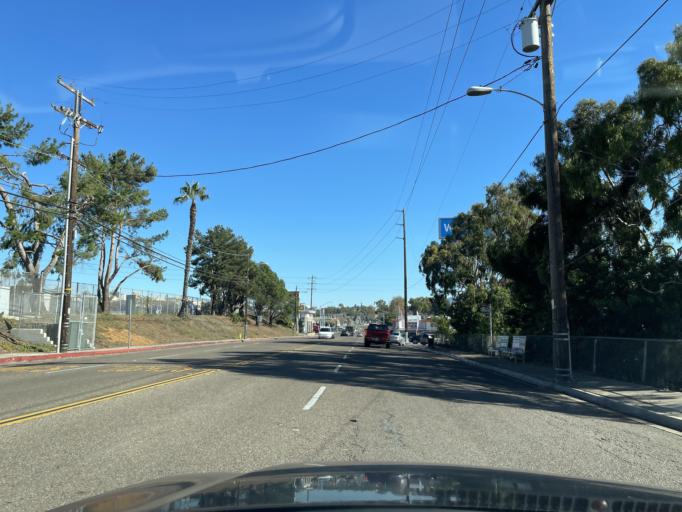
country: US
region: California
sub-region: San Diego County
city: National City
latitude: 32.6759
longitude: -117.0999
